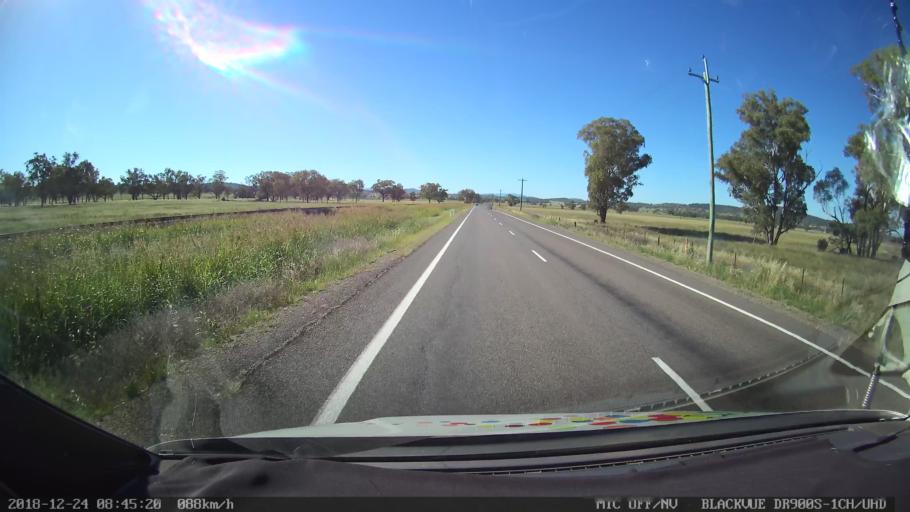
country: AU
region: New South Wales
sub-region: Liverpool Plains
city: Quirindi
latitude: -31.4137
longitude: 150.6516
